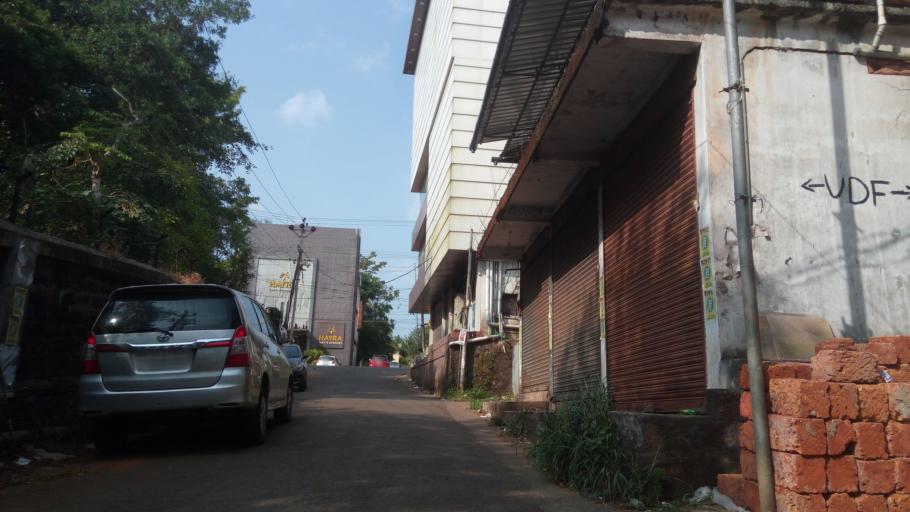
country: IN
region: Kerala
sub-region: Malappuram
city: Malappuram
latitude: 10.9995
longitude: 75.9998
